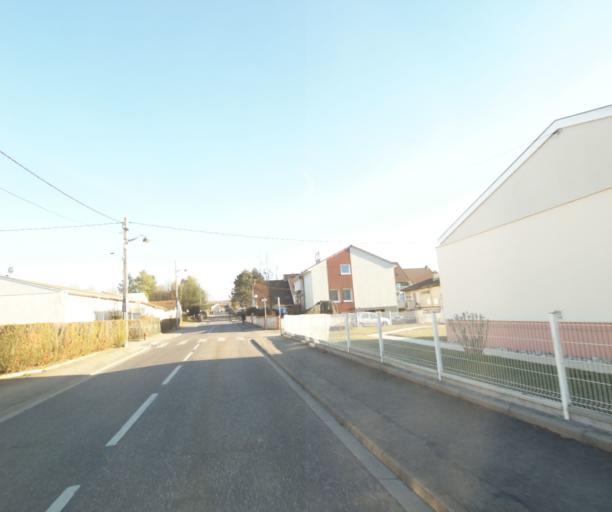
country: FR
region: Lorraine
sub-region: Departement de Meurthe-et-Moselle
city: Seichamps
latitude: 48.7131
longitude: 6.2618
